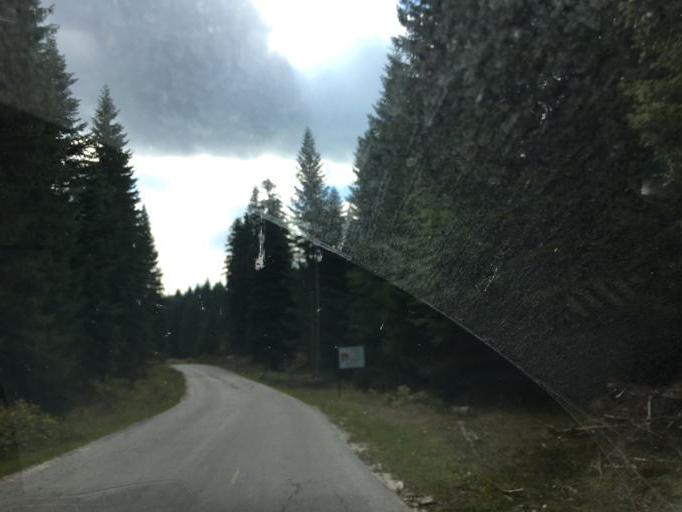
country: BG
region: Pazardzhik
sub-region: Obshtina Batak
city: Batak
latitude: 41.9091
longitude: 24.2936
